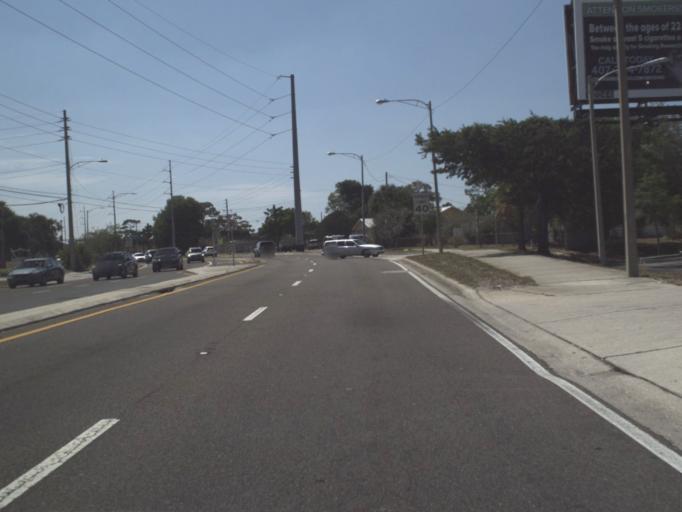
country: US
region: Florida
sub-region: Orange County
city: Azalea Park
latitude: 28.5241
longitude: -81.3116
